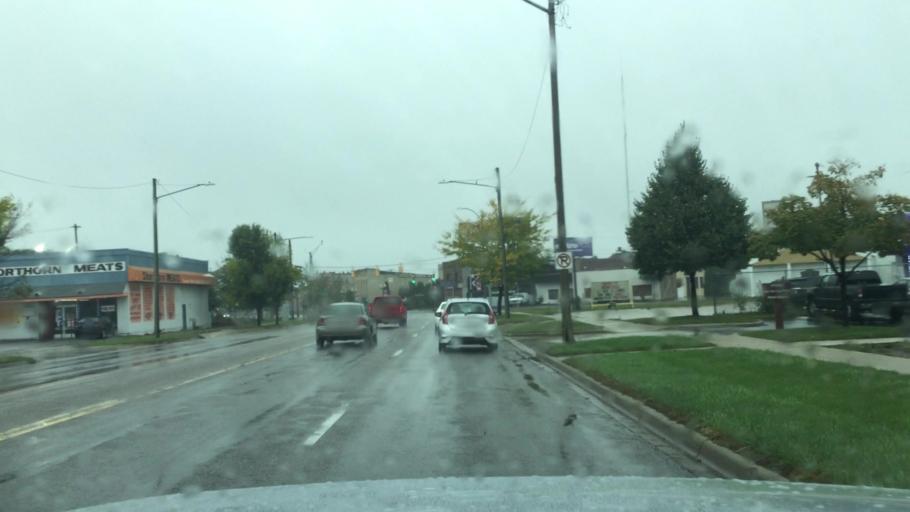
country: US
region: Michigan
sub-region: Saginaw County
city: Saginaw
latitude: 43.4282
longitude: -83.9305
